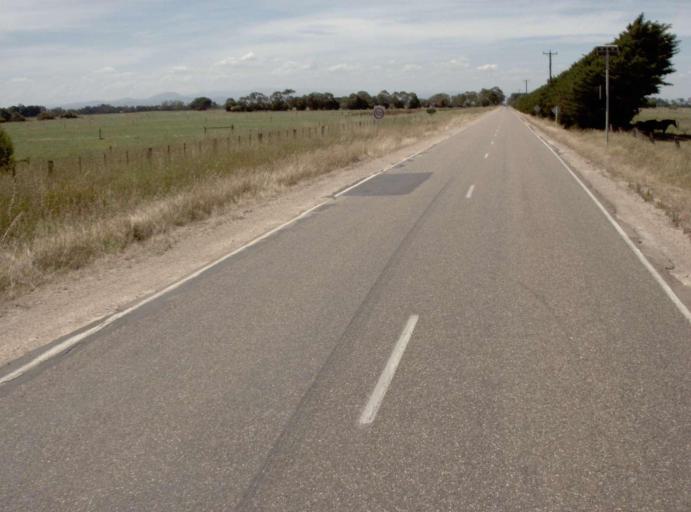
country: AU
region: Victoria
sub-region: Wellington
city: Heyfield
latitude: -38.0537
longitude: 146.8743
